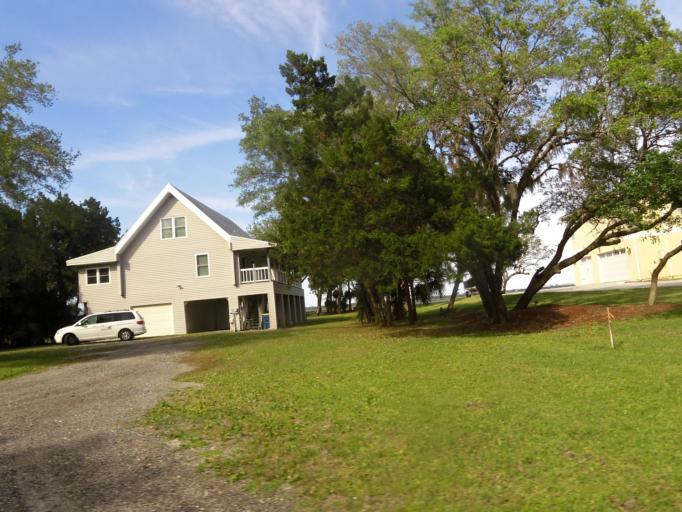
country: US
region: Florida
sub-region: Nassau County
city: Fernandina Beach
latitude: 30.5340
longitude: -81.4842
